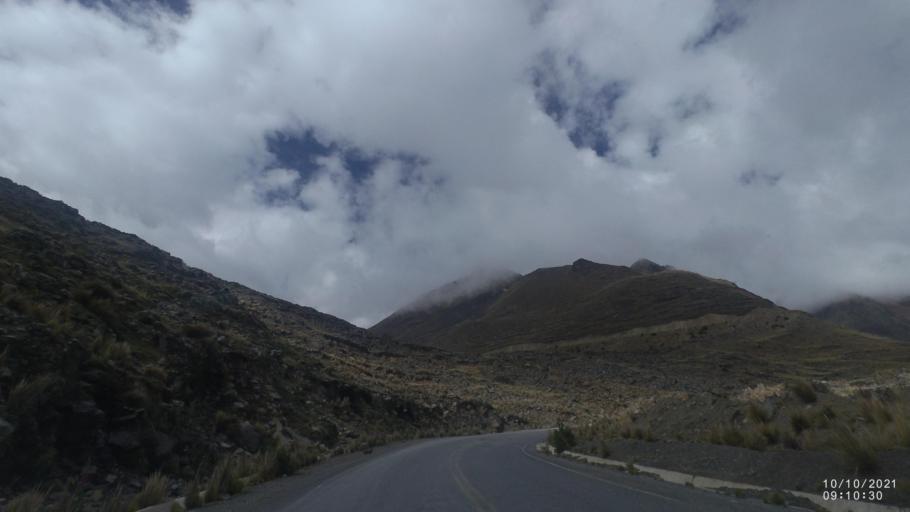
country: BO
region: La Paz
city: Quime
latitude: -17.0273
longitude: -67.2837
